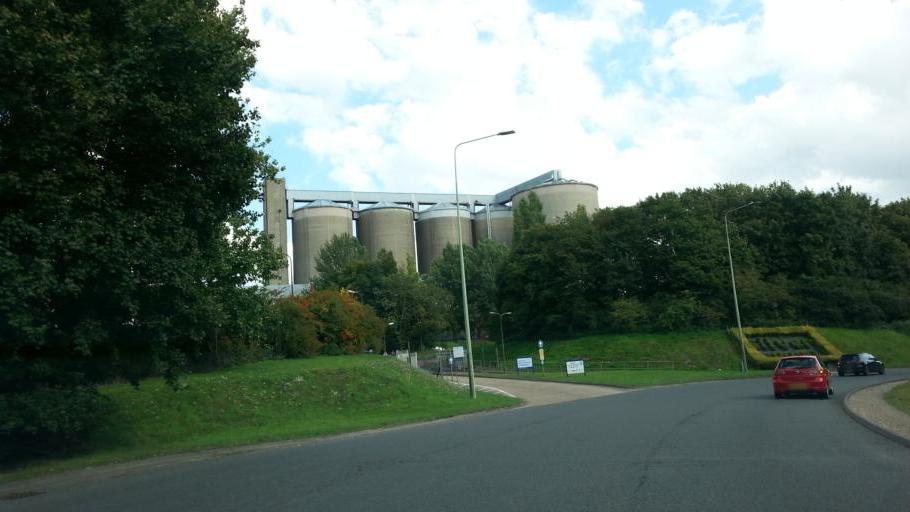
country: GB
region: England
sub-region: Suffolk
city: Bury St Edmunds
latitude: 52.2559
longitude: 0.7190
